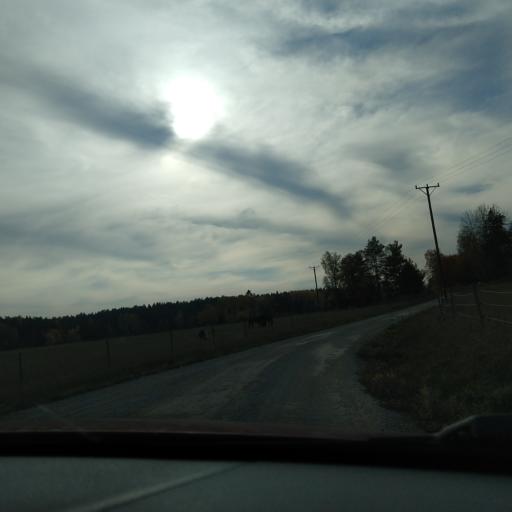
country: SE
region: Stockholm
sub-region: Vallentuna Kommun
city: Vallentuna
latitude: 59.5360
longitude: 18.0153
